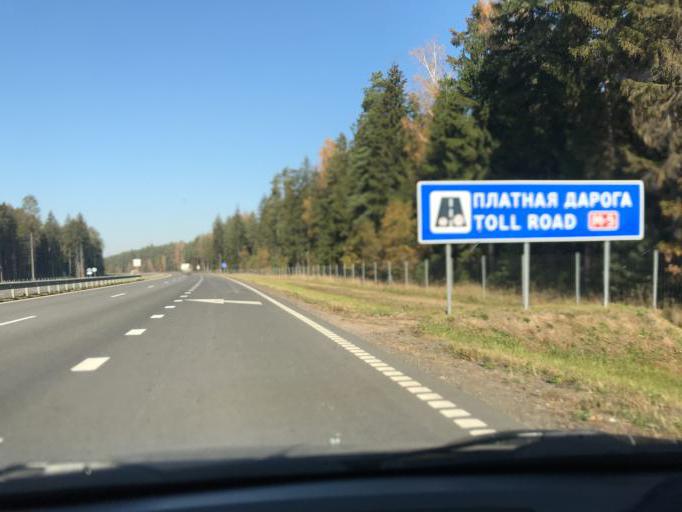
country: BY
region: Mogilev
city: Kirawsk
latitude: 53.2198
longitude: 29.3409
